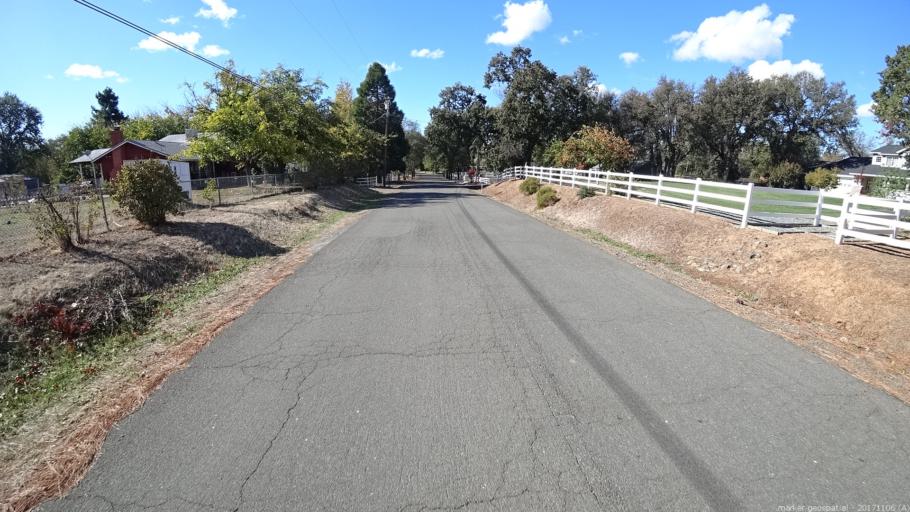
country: US
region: California
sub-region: Shasta County
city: Palo Cedro
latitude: 40.5770
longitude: -122.2224
